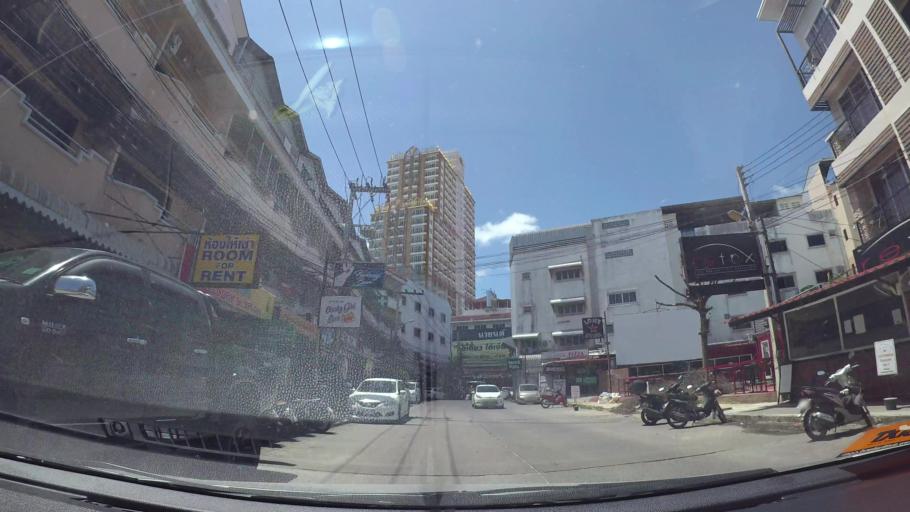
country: TH
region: Chon Buri
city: Phatthaya
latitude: 12.9277
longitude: 100.8864
